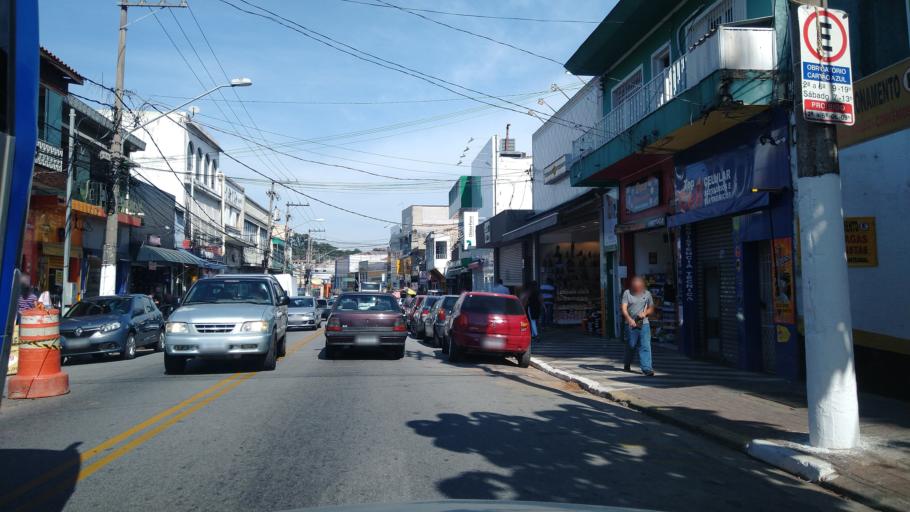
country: BR
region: Sao Paulo
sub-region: Sao Paulo
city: Sao Paulo
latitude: -23.4721
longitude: -46.6666
